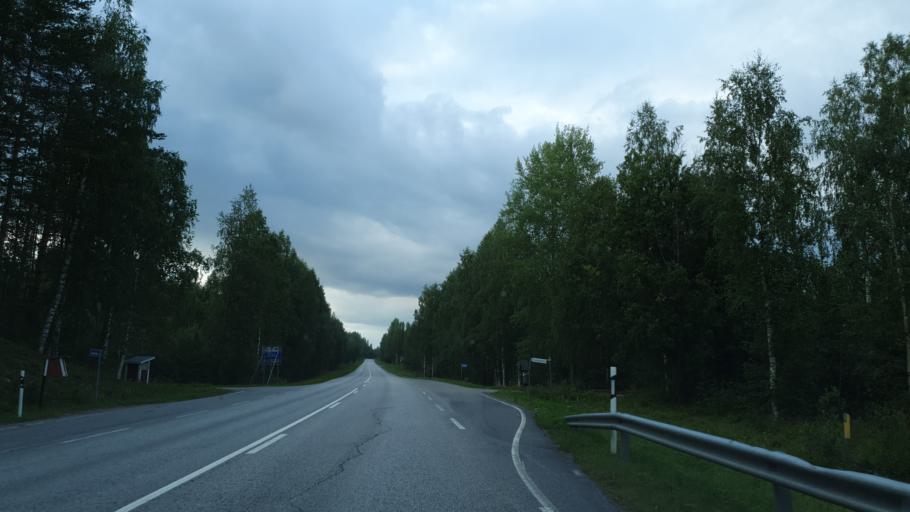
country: FI
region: North Karelia
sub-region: Joensuu
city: Eno
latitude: 63.0487
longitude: 30.1263
